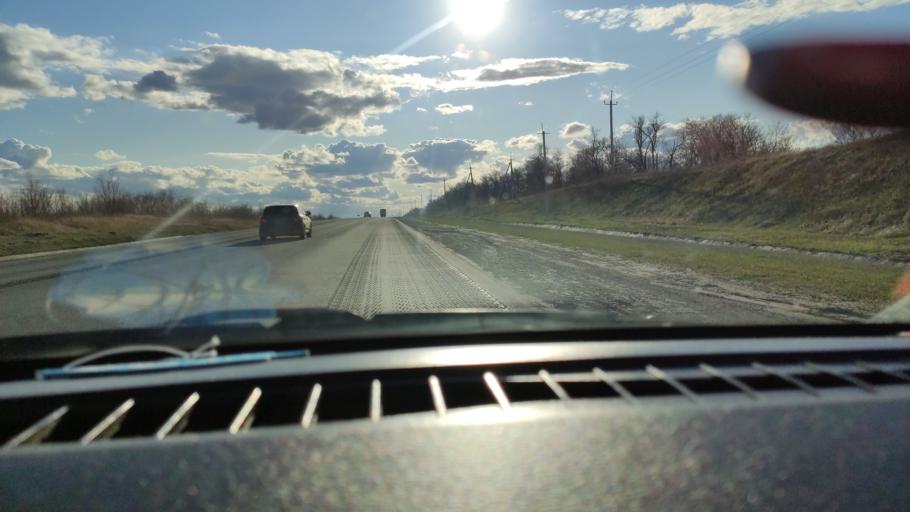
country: RU
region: Saratov
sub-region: Saratovskiy Rayon
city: Saratov
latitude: 51.7763
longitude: 46.1049
